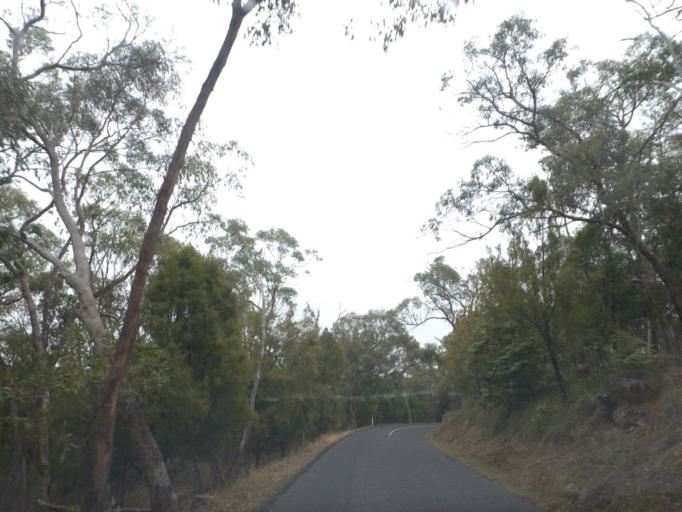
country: AU
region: Victoria
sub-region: Nillumbik
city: Saint Andrews
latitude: -37.6092
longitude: 145.2960
